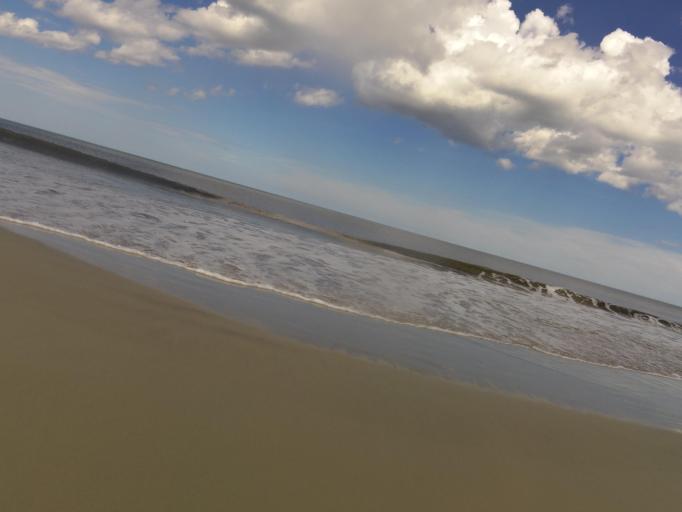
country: US
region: Florida
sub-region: Nassau County
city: Fernandina Beach
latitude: 30.6888
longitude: -81.4276
